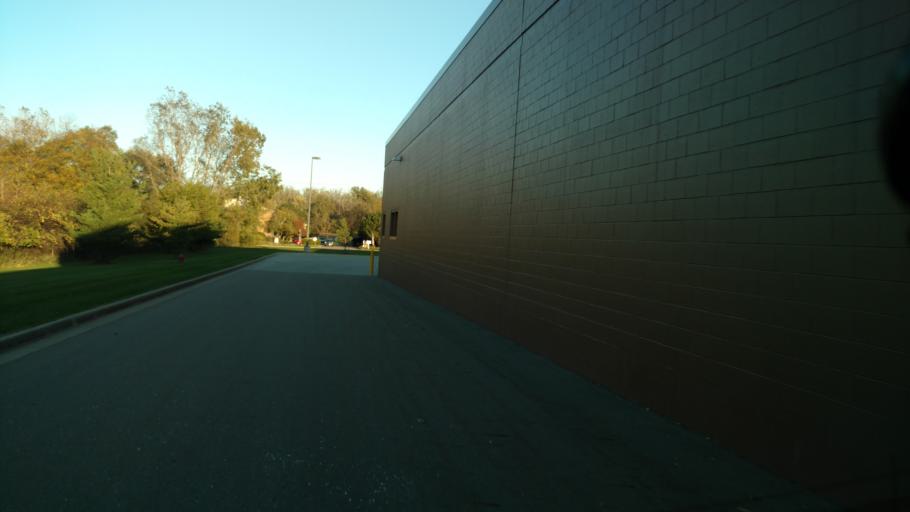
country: US
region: Michigan
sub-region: Ingham County
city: East Lansing
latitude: 42.7637
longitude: -84.5002
